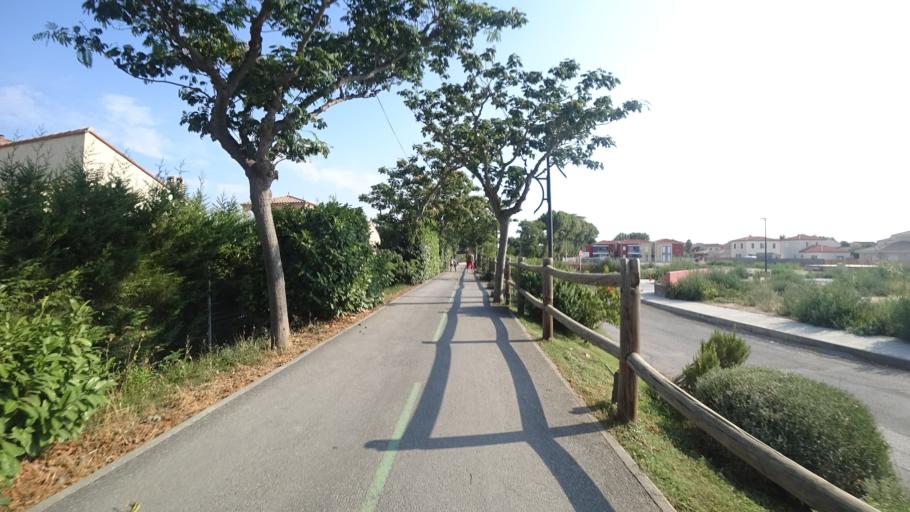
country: FR
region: Languedoc-Roussillon
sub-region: Departement des Pyrenees-Orientales
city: Claira
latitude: 42.7578
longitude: 2.9511
